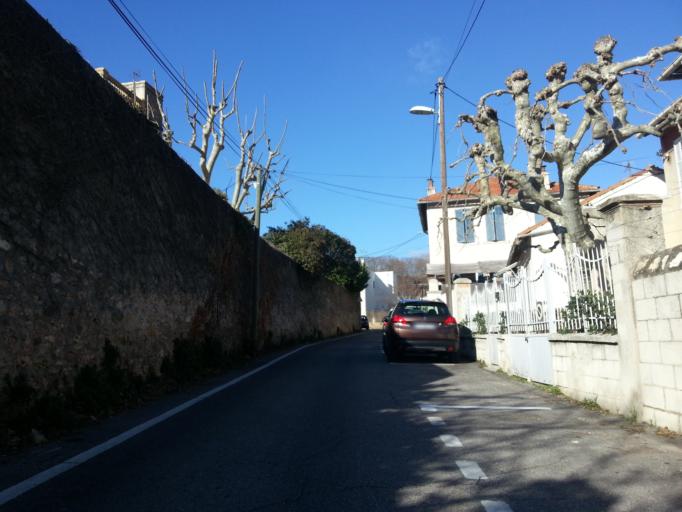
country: FR
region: Provence-Alpes-Cote d'Azur
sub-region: Departement des Bouches-du-Rhone
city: Marseille 04
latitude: 43.3013
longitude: 5.4181
